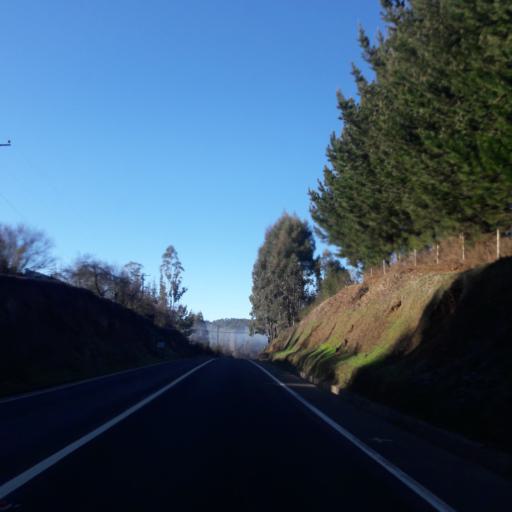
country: CL
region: Biobio
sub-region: Provincia de Biobio
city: La Laja
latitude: -37.2856
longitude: -72.9384
